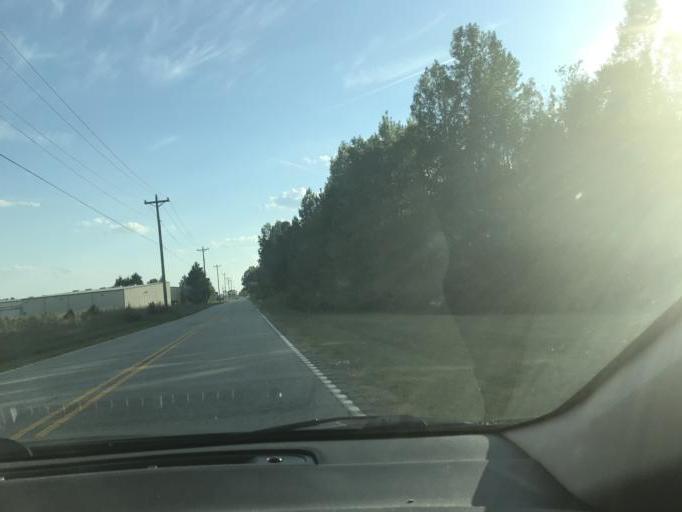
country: US
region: South Carolina
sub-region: Cherokee County
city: Gaffney
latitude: 35.0951
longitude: -81.6899
